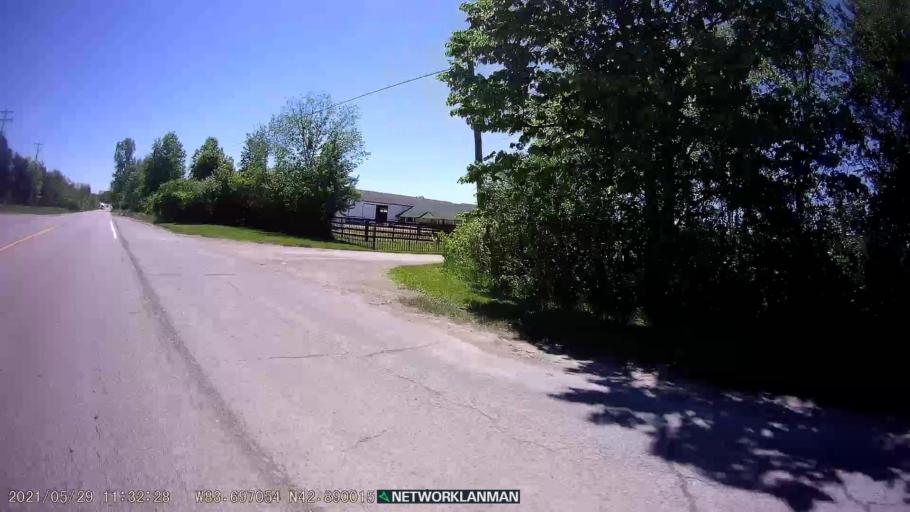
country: US
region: Michigan
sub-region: Genesee County
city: Lake Fenton
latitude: 42.8898
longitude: -83.6970
